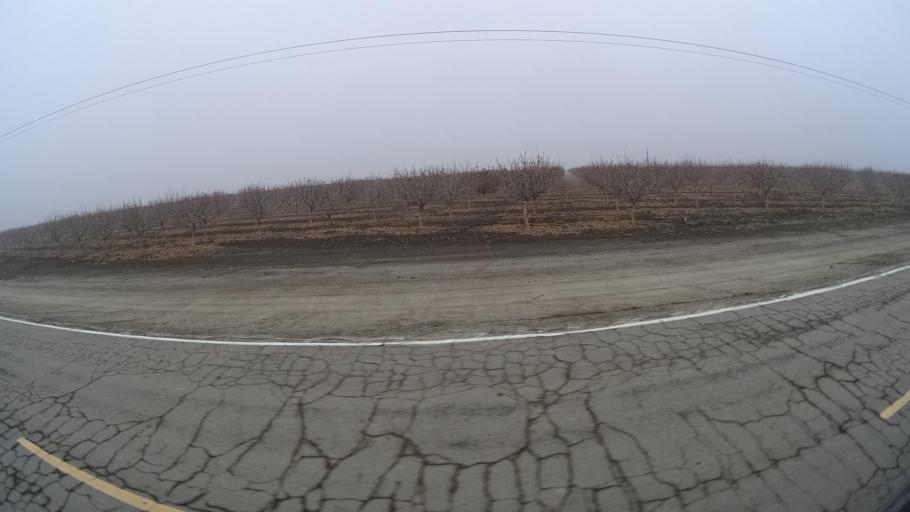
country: US
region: California
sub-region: Kern County
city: Lost Hills
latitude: 35.5186
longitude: -119.6177
